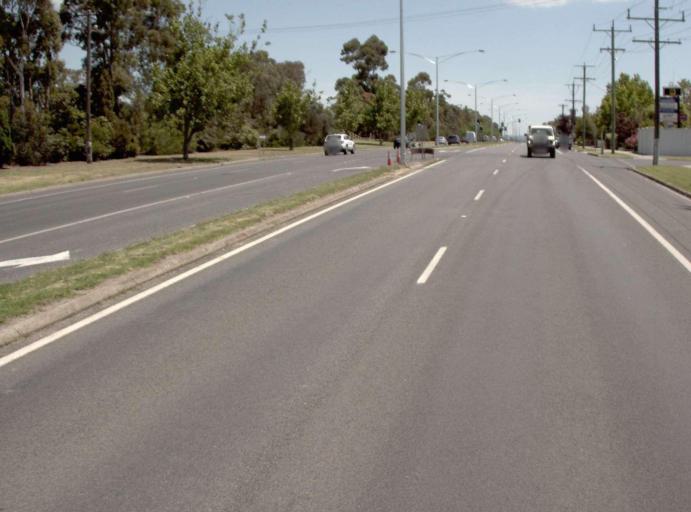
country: AU
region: Victoria
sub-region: Latrobe
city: Traralgon
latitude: -38.2015
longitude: 146.5253
